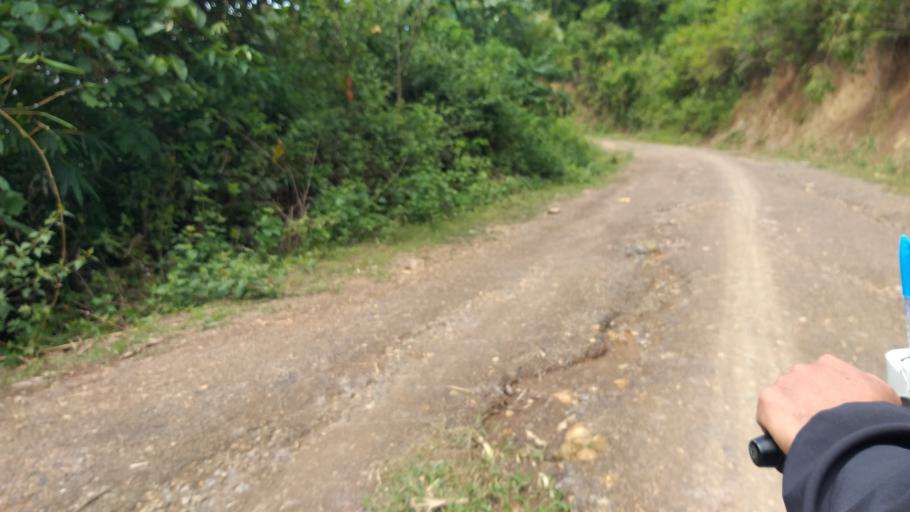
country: VN
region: Huyen Dien Bien
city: Dien Bien Phu
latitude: 21.4712
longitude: 102.6806
